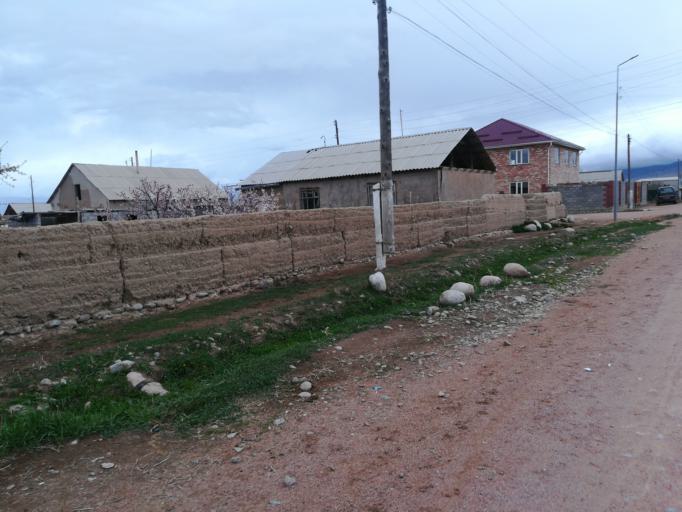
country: KG
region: Ysyk-Koel
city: Bokombayevskoye
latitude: 42.1083
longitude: 76.9802
